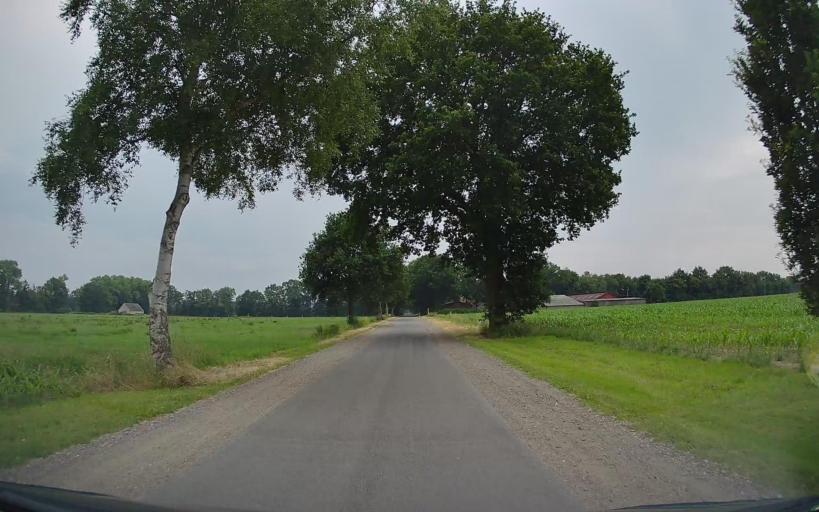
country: DE
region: Lower Saxony
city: Friesoythe
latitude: 53.0213
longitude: 7.9036
